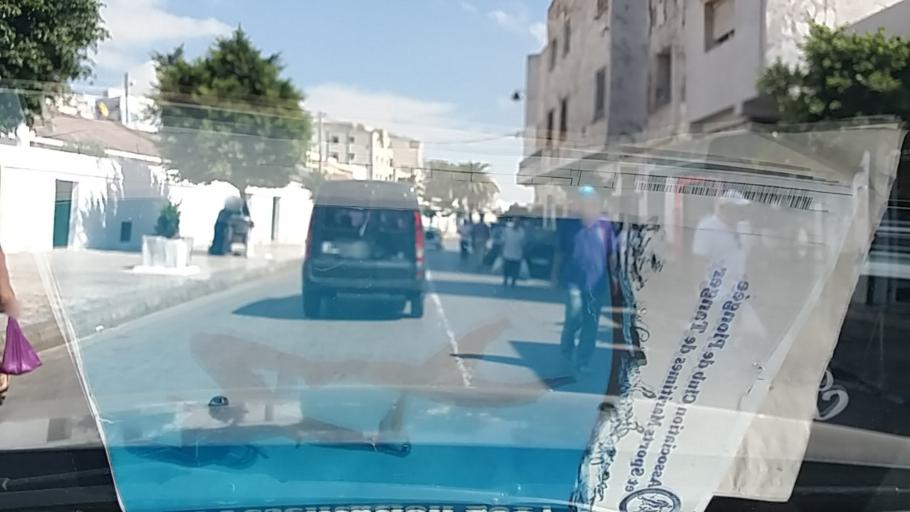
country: MA
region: Tanger-Tetouan
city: Tetouan
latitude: 35.5744
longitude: -5.3874
